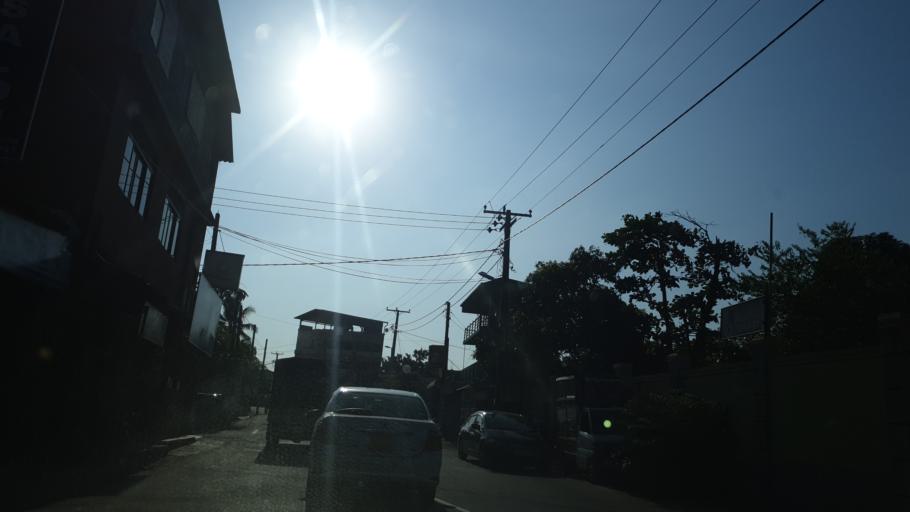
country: LK
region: Western
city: Sri Jayewardenepura Kotte
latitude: 6.8690
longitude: 79.9114
